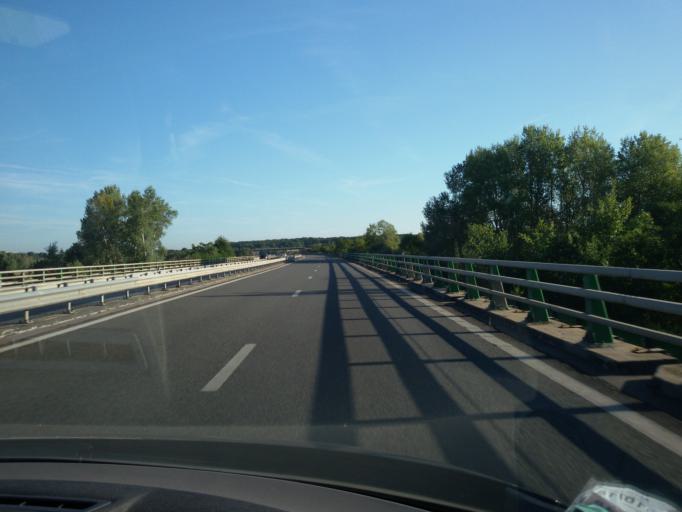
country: FR
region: Centre
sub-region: Departement du Cher
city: Orval
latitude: 46.7865
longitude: 2.4123
